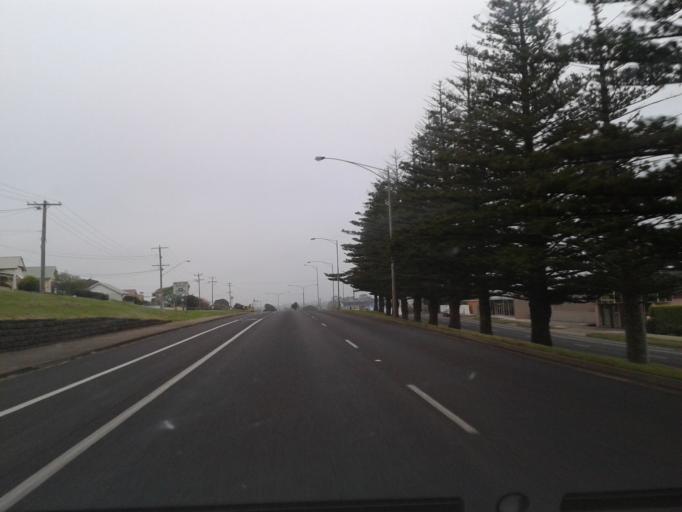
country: AU
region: Victoria
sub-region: Warrnambool
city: Warrnambool
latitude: -38.3731
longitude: 142.4758
